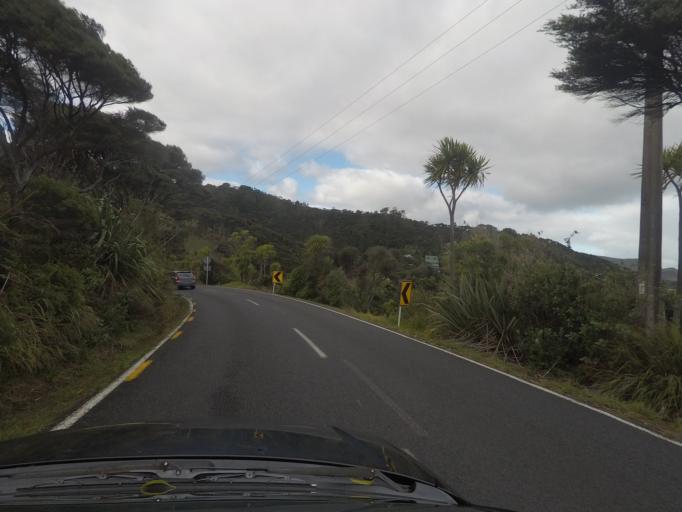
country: NZ
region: Auckland
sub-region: Auckland
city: Muriwai Beach
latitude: -36.8774
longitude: 174.4513
